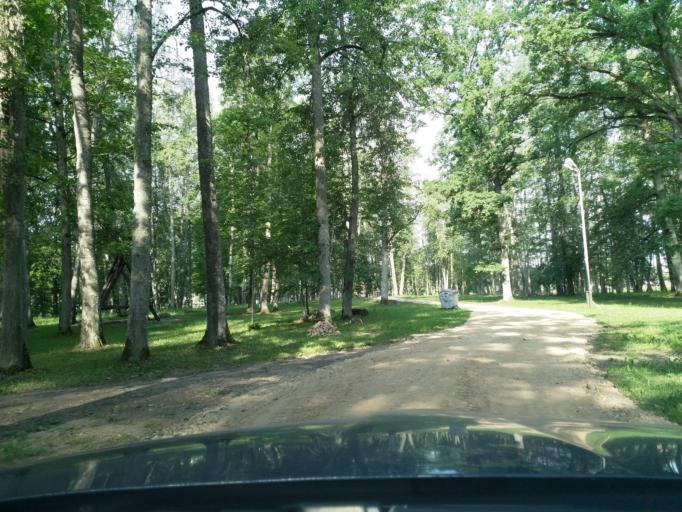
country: LV
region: Talsu Rajons
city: Sabile
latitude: 56.9519
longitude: 22.4025
